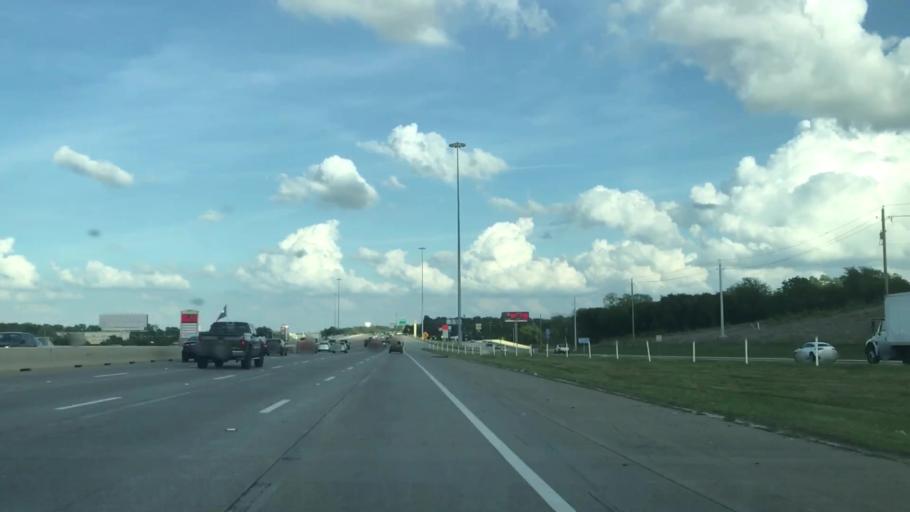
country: US
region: Texas
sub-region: Dallas County
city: Grand Prairie
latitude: 32.7590
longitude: -97.0026
